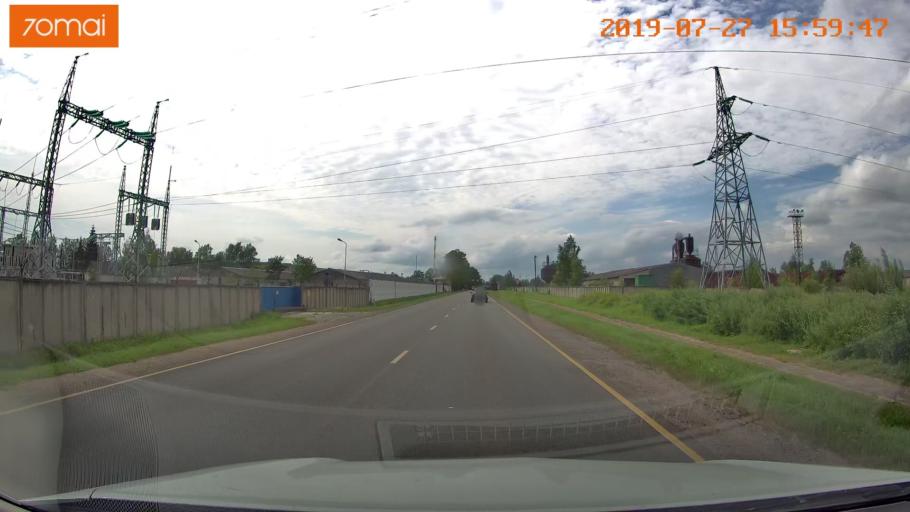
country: RU
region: Kaliningrad
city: Chernyakhovsk
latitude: 54.6268
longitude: 21.8459
